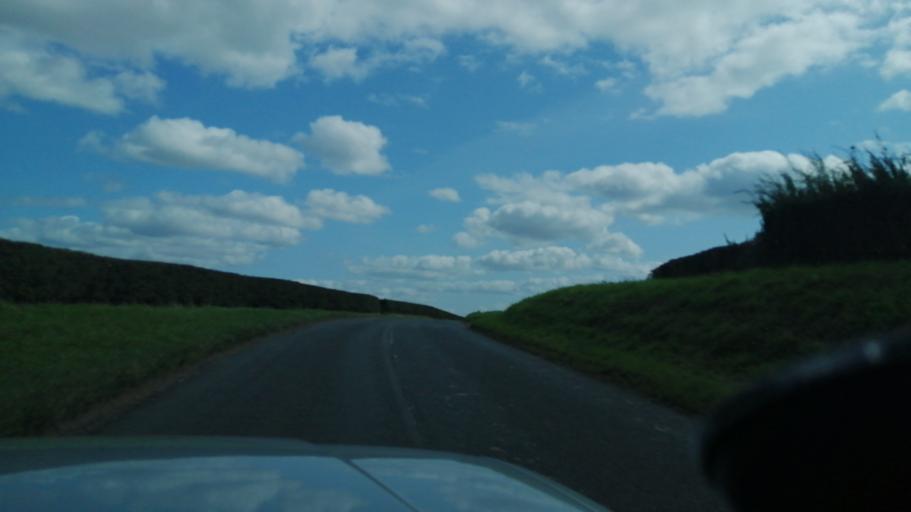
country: GB
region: England
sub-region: Herefordshire
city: Kingstone
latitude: 52.0115
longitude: -2.8336
